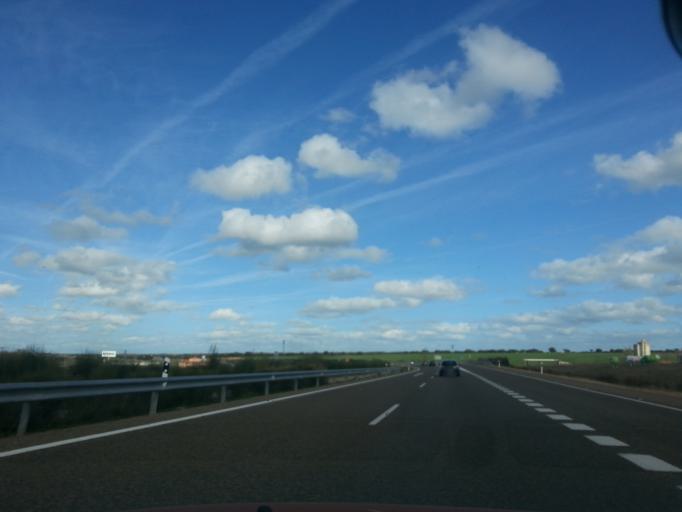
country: ES
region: Castille and Leon
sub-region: Provincia de Salamanca
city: Aldehuela de la Boveda
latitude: 40.8474
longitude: -6.0563
